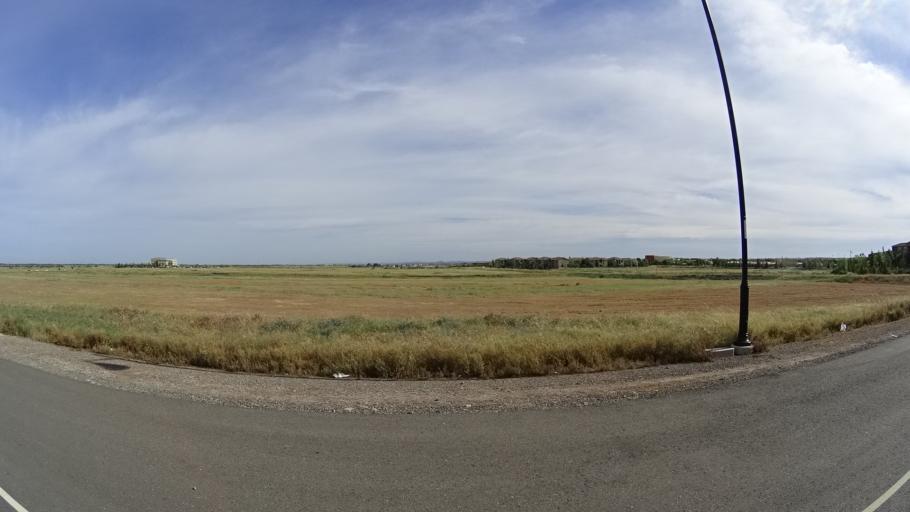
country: US
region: California
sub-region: Placer County
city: Lincoln
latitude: 38.8315
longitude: -121.2949
